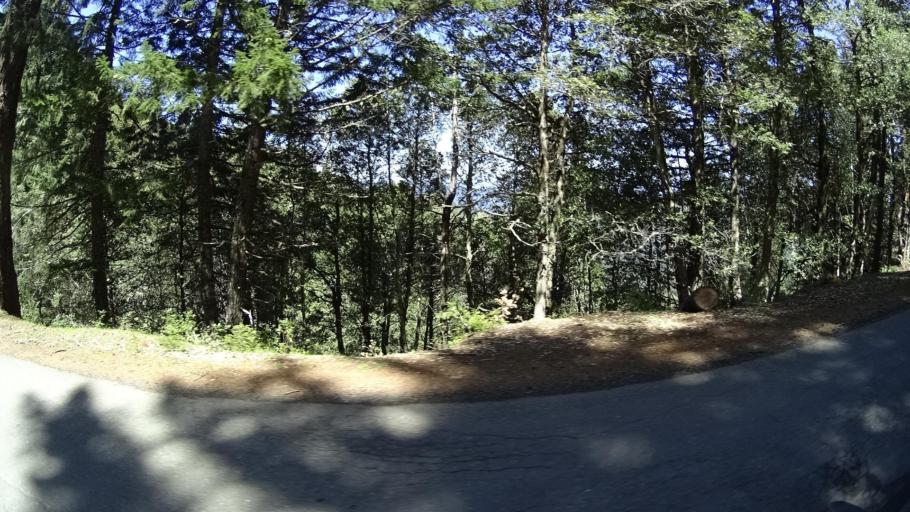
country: US
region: California
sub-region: Humboldt County
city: Rio Dell
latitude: 40.2919
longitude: -124.0567
